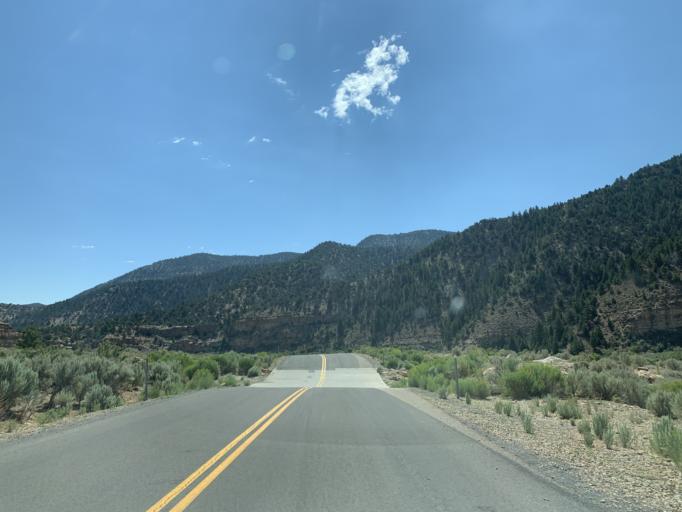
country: US
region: Utah
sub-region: Carbon County
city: East Carbon City
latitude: 39.7776
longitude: -110.4367
